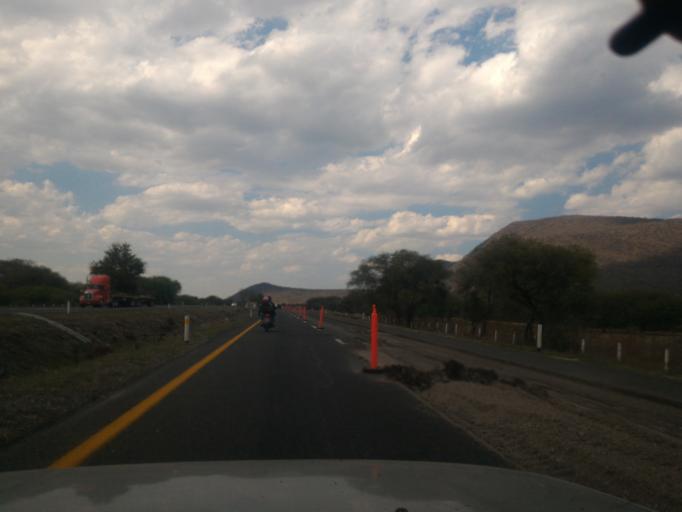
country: MX
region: Jalisco
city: Zacoalco de Torres
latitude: 20.1743
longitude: -103.5081
